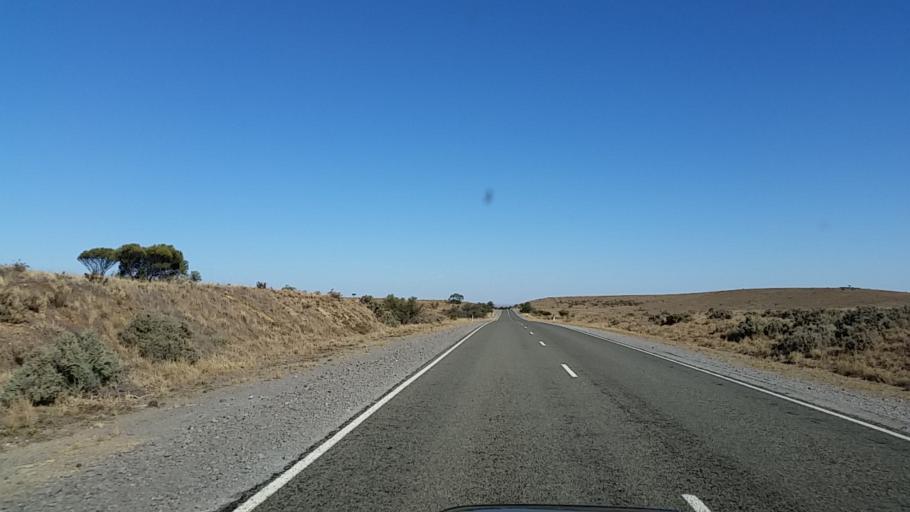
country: AU
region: South Australia
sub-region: Peterborough
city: Peterborough
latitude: -32.6072
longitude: 138.5692
